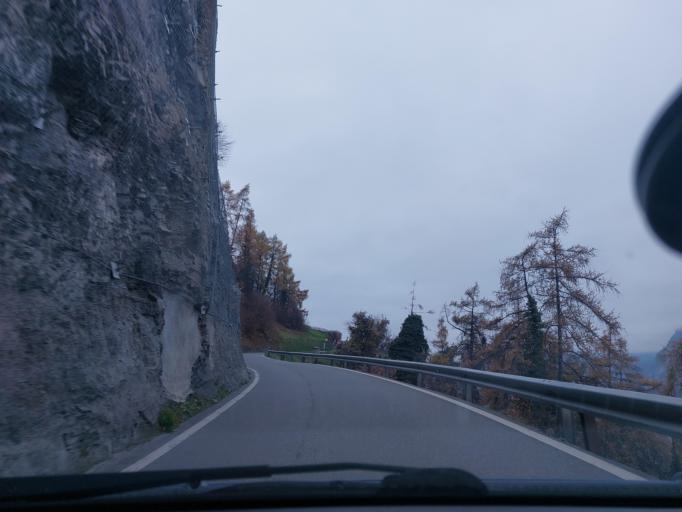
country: CH
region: Valais
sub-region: Conthey District
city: Ardon
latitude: 46.1925
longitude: 7.2800
